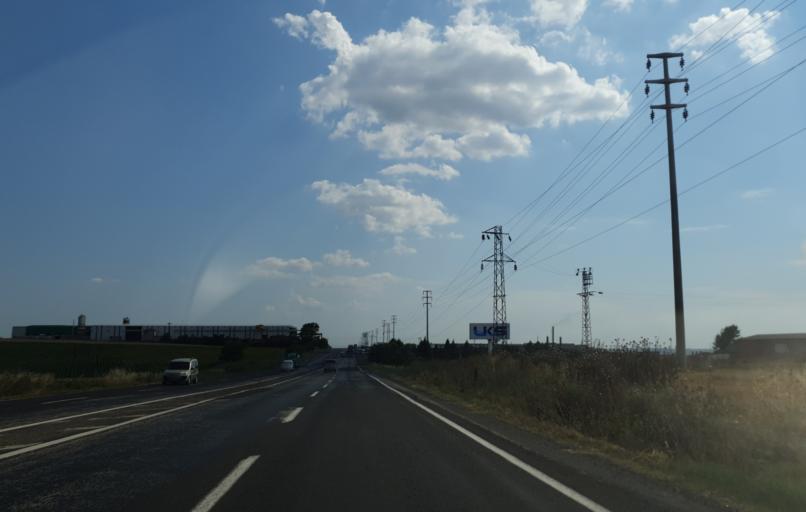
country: TR
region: Kirklareli
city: Buyukkaristiran
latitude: 41.2550
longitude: 27.5443
